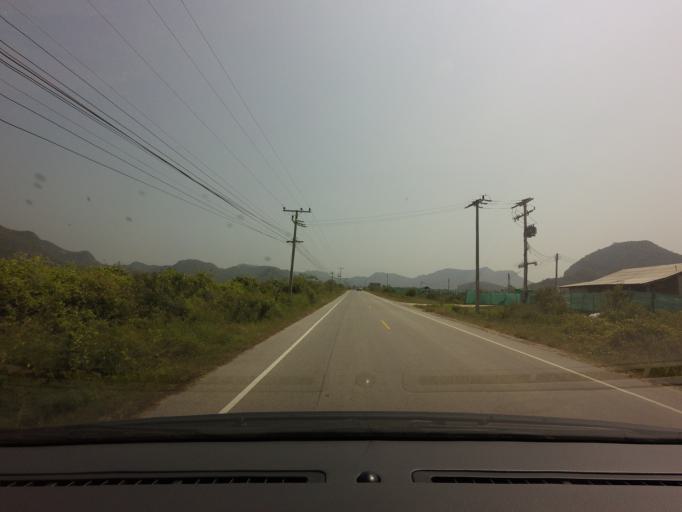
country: TH
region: Prachuap Khiri Khan
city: Sam Roi Yot
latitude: 12.1959
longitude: 99.9813
